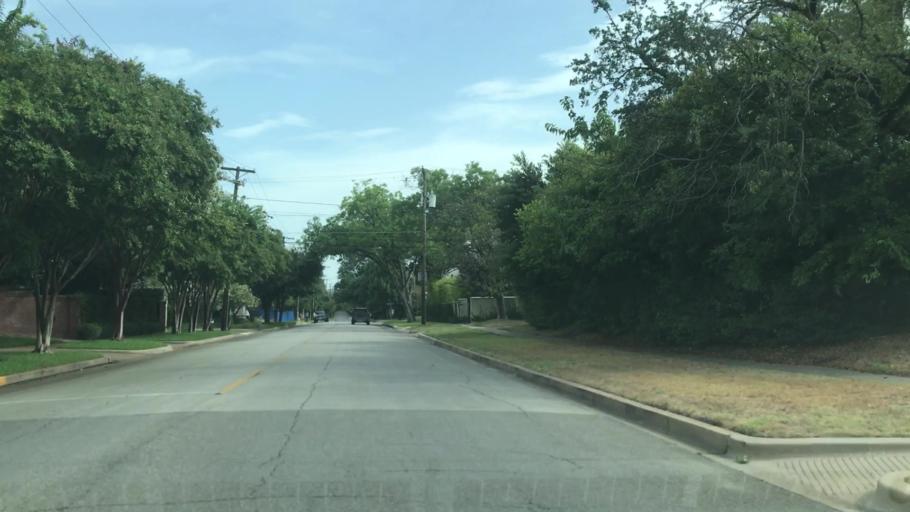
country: US
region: Texas
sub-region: Dallas County
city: Highland Park
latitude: 32.8249
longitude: -96.8070
